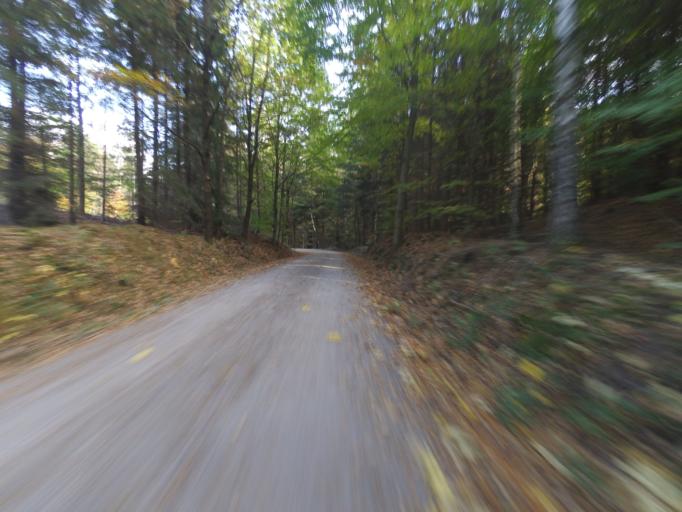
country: DE
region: Saxony
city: Albertstadt
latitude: 51.1010
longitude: 13.8124
